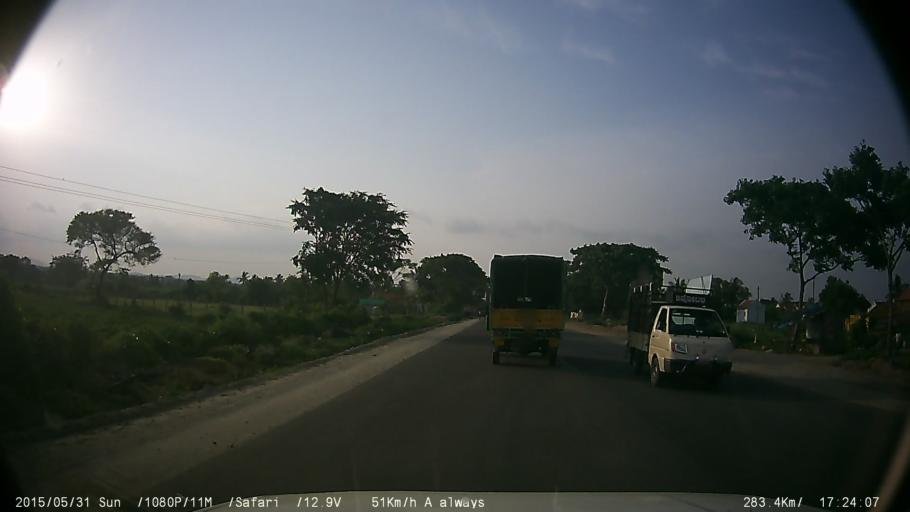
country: IN
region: Karnataka
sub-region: Chamrajnagar
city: Gundlupet
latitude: 11.8461
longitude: 76.6725
